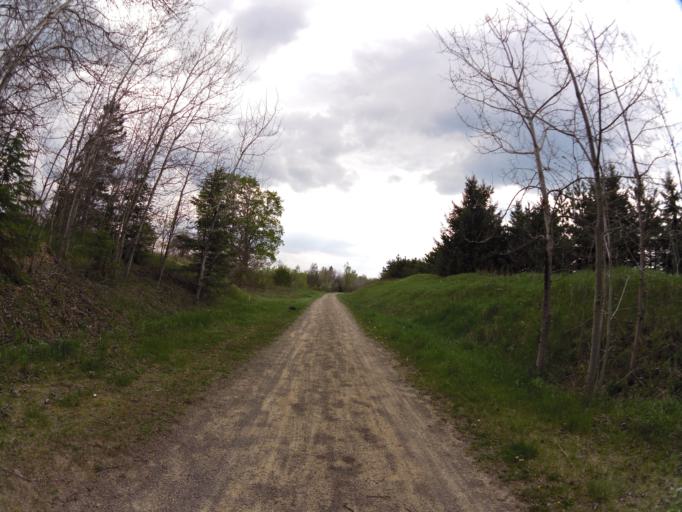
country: CA
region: Ontario
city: Brampton
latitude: 43.8354
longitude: -79.8927
